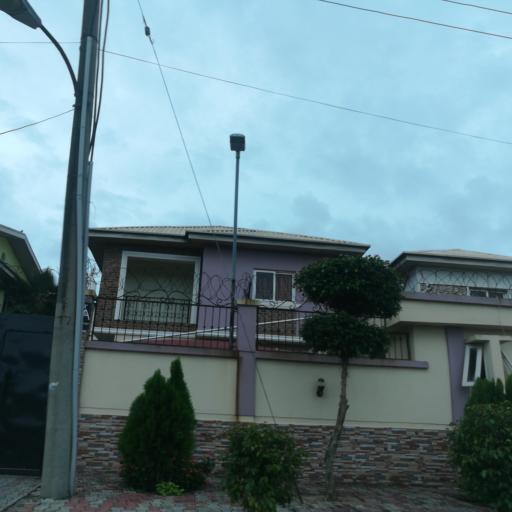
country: NG
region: Lagos
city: Ikoyi
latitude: 6.4410
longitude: 3.4700
